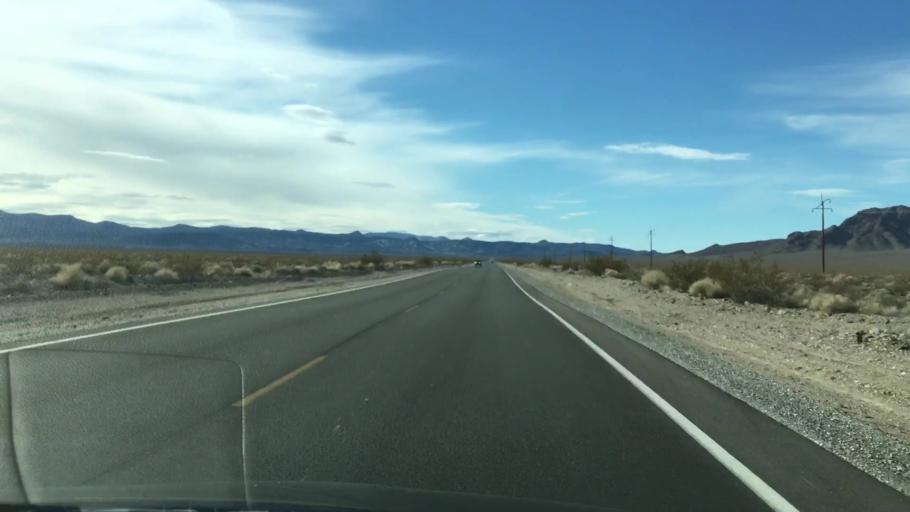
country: US
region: Nevada
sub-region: Nye County
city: Pahrump
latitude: 36.3043
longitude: -116.4428
